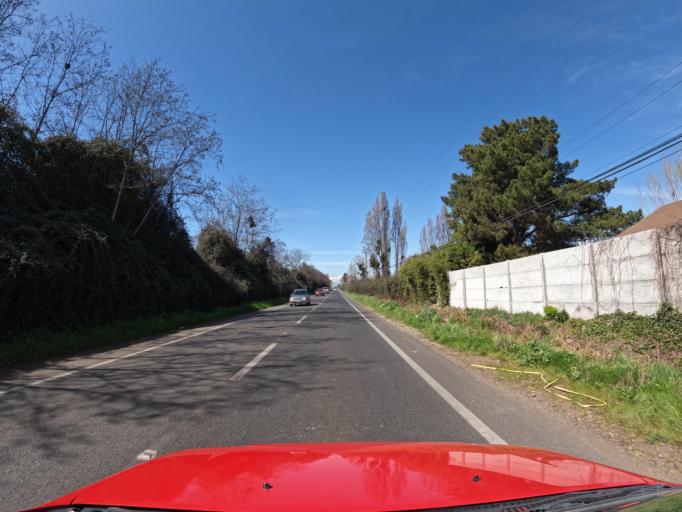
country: CL
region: Maule
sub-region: Provincia de Curico
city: Teno
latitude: -34.9639
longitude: -71.0642
